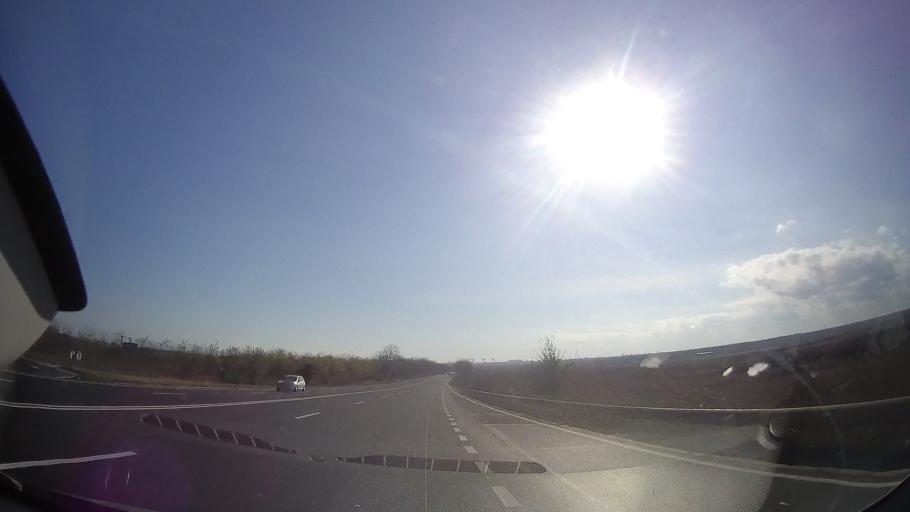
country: RO
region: Constanta
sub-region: Municipiul Mangalia
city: Mangalia
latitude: 43.8557
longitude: 28.5760
